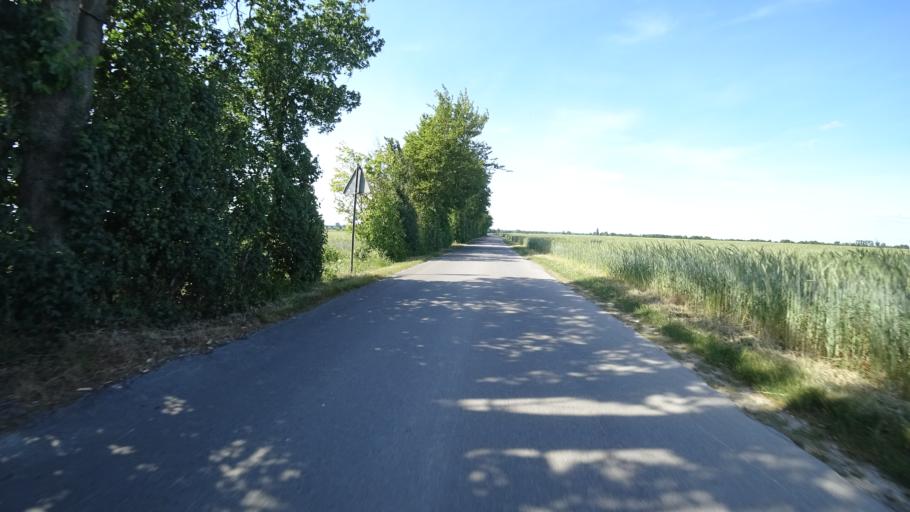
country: DE
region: North Rhine-Westphalia
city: Erwitte
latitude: 51.6095
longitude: 8.3698
